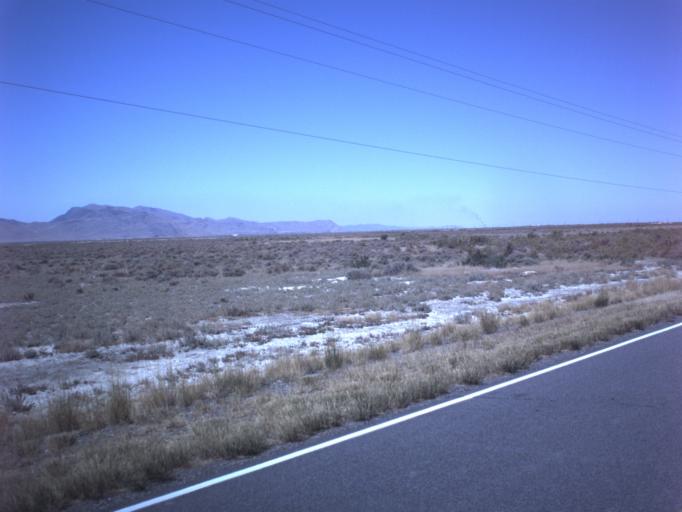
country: US
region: Utah
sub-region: Tooele County
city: Grantsville
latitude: 40.7233
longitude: -112.6595
